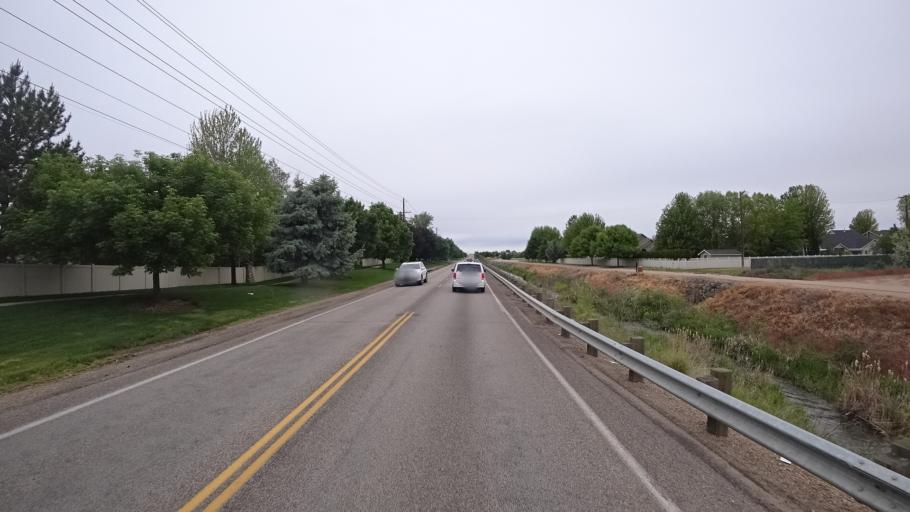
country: US
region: Idaho
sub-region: Ada County
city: Meridian
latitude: 43.6339
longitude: -116.4177
